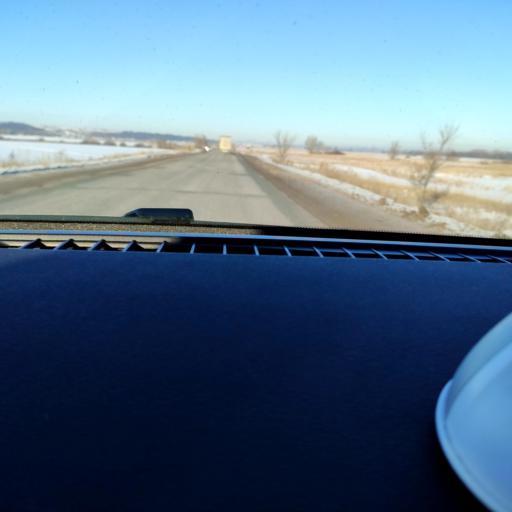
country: RU
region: Samara
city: Spiridonovka
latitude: 53.1318
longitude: 50.6129
